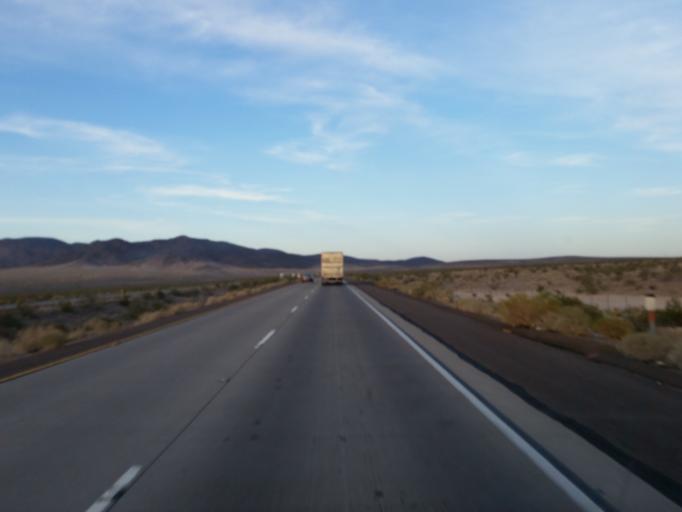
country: US
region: California
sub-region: San Bernardino County
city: Twentynine Palms
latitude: 34.7266
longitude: -116.1257
